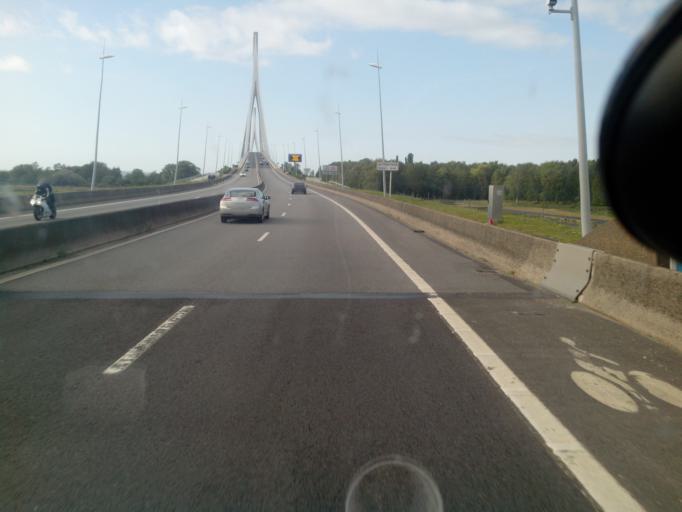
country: FR
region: Lower Normandy
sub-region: Departement du Calvados
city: La Riviere-Saint-Sauveur
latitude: 49.4204
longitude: 0.2756
